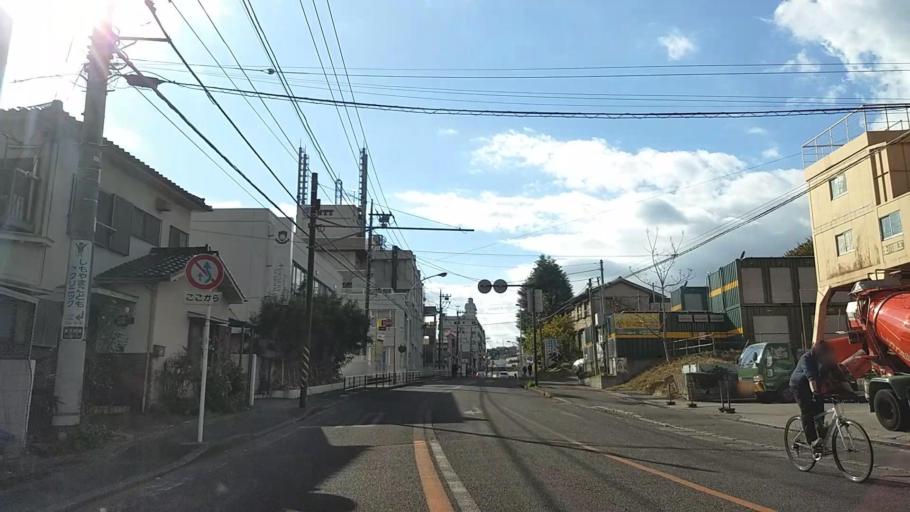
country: JP
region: Tokyo
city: Chofugaoka
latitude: 35.6105
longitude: 139.5190
